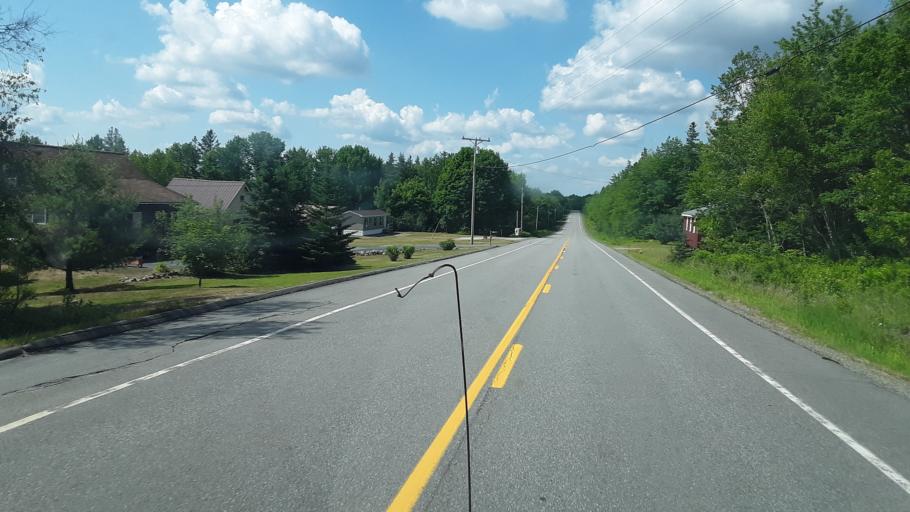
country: US
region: Maine
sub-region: Washington County
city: Machias
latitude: 45.0041
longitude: -67.5529
